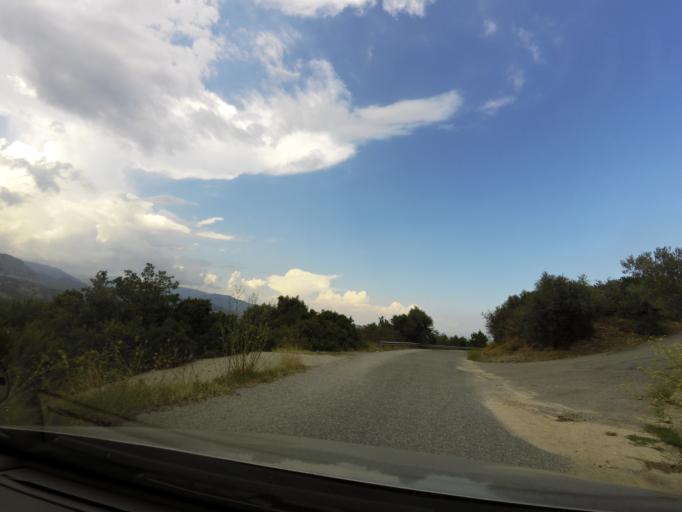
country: IT
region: Calabria
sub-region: Provincia di Reggio Calabria
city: Camini
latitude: 38.4375
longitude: 16.5093
